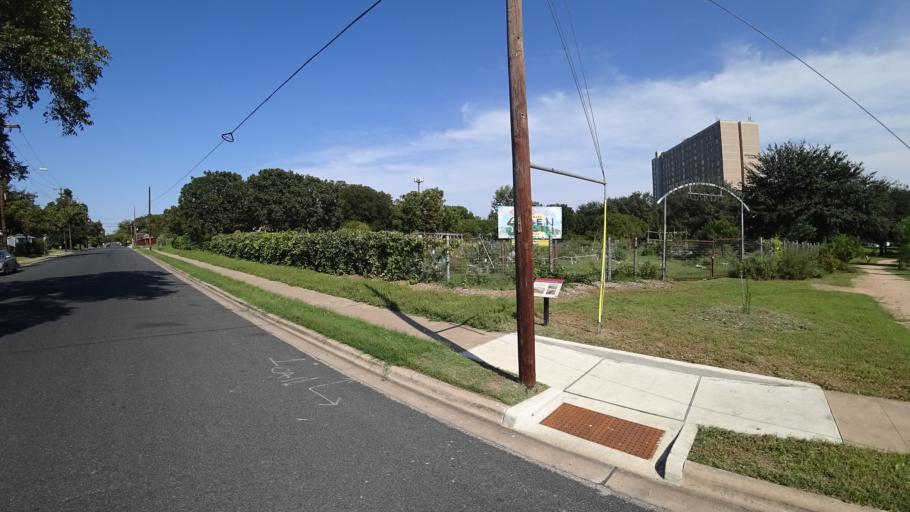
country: US
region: Texas
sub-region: Travis County
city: Austin
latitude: 30.2535
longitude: -97.7355
